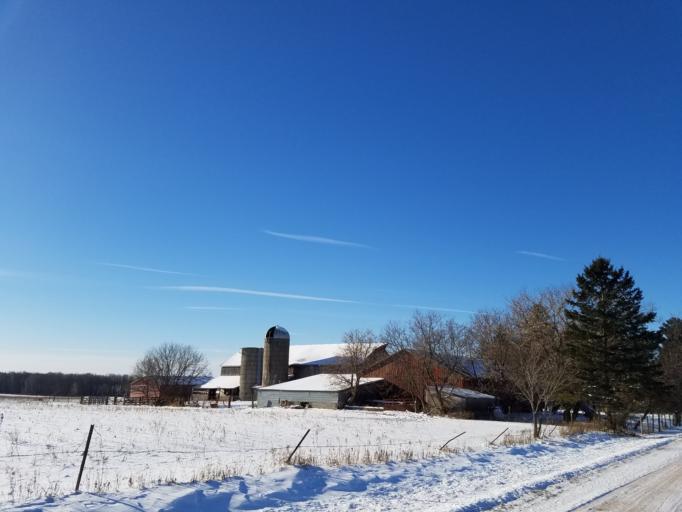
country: US
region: Wisconsin
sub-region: Marathon County
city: Spencer
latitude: 44.6123
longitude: -90.3676
